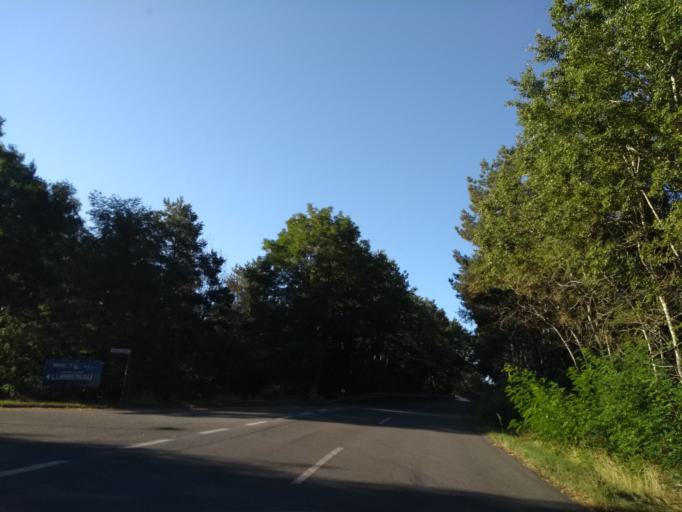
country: DE
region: Brandenburg
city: Lubbenau
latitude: 51.8410
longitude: 13.9508
